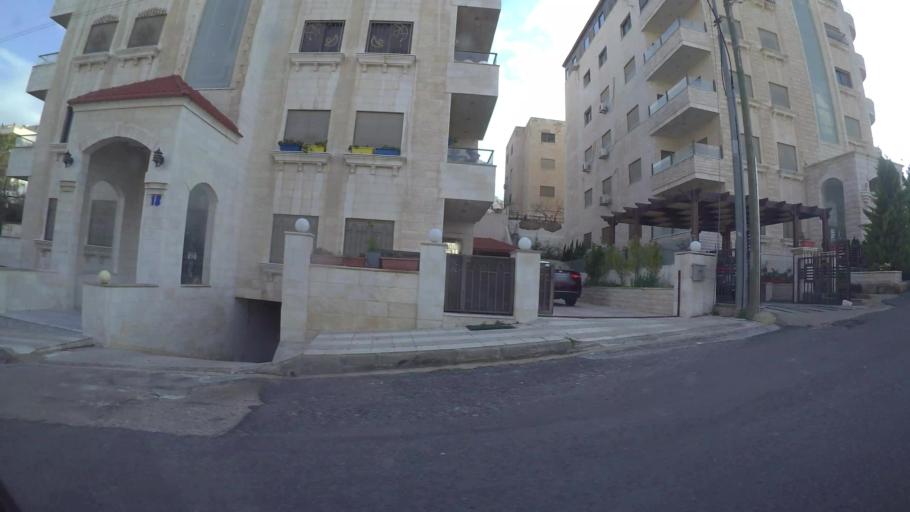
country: JO
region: Amman
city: Al Jubayhah
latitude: 32.0028
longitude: 35.8719
